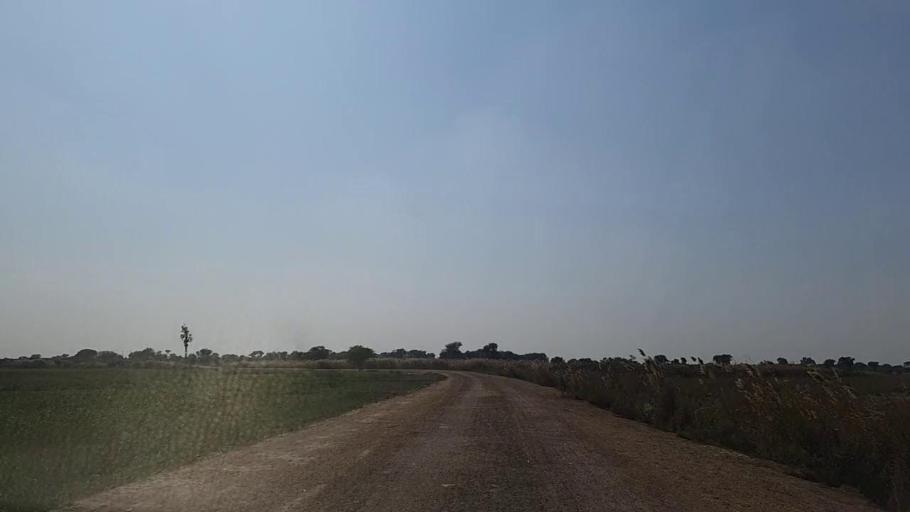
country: PK
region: Sindh
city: Daur
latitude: 26.4941
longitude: 68.2613
